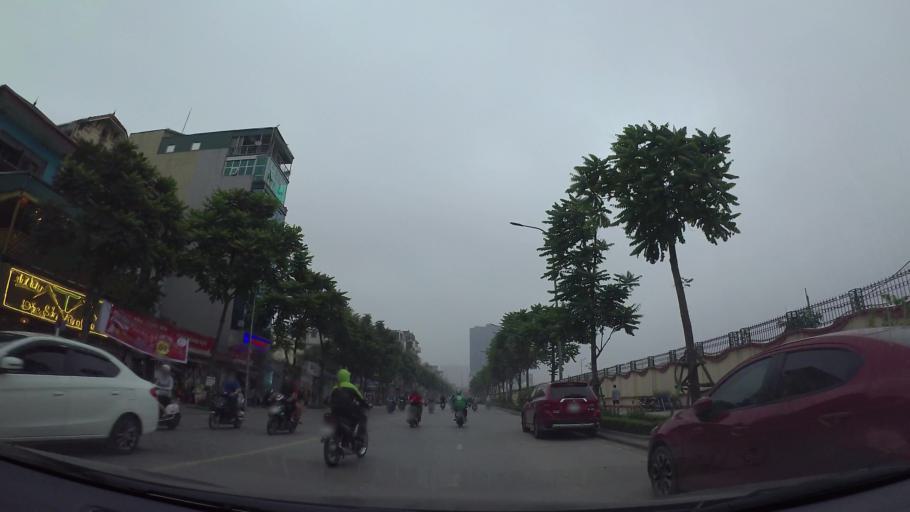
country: VN
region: Ha Noi
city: Hai BaTrung
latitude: 20.9947
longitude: 105.8310
